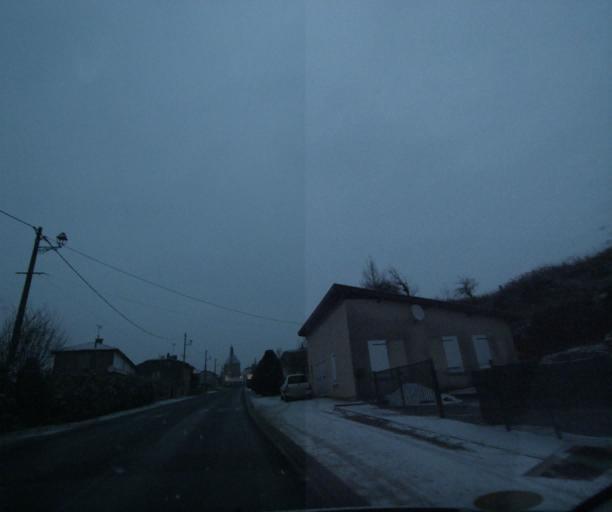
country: FR
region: Champagne-Ardenne
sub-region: Departement de la Haute-Marne
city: Wassy
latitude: 48.4256
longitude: 4.9608
